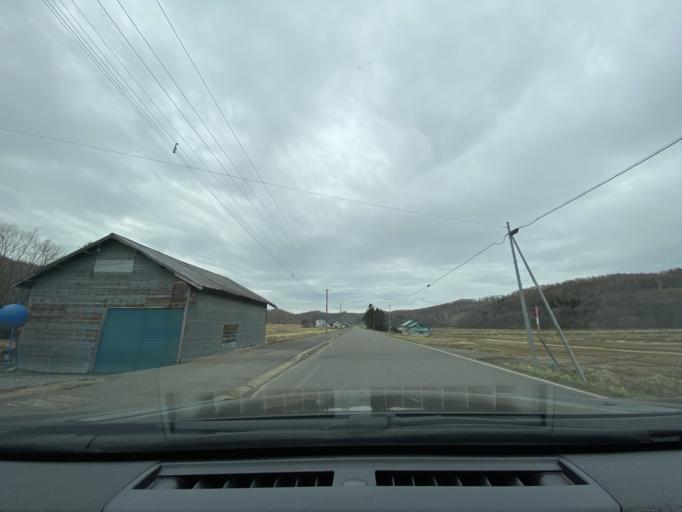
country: JP
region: Hokkaido
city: Nayoro
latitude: 44.0831
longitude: 142.4183
